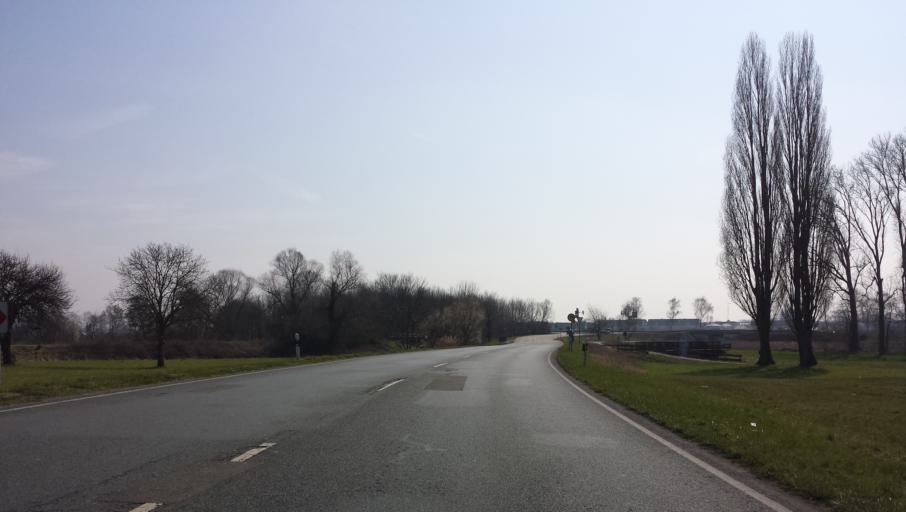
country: DE
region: Baden-Wuerttemberg
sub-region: Karlsruhe Region
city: Reilingen
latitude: 49.3067
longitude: 8.5628
